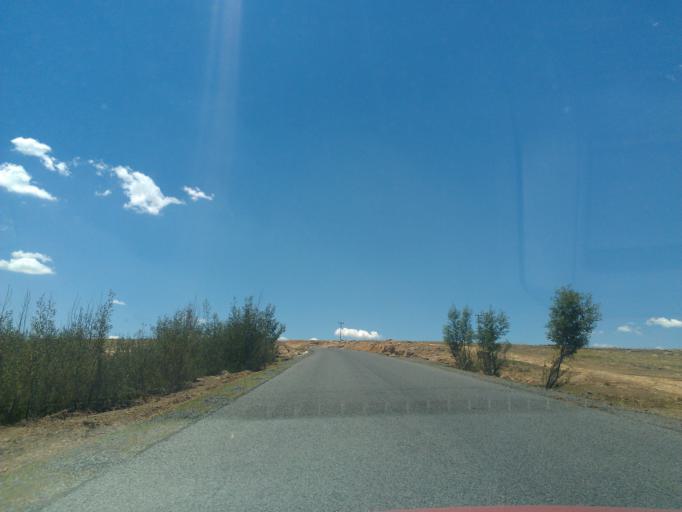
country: LS
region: Berea
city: Teyateyaneng
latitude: -29.1031
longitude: 27.8455
